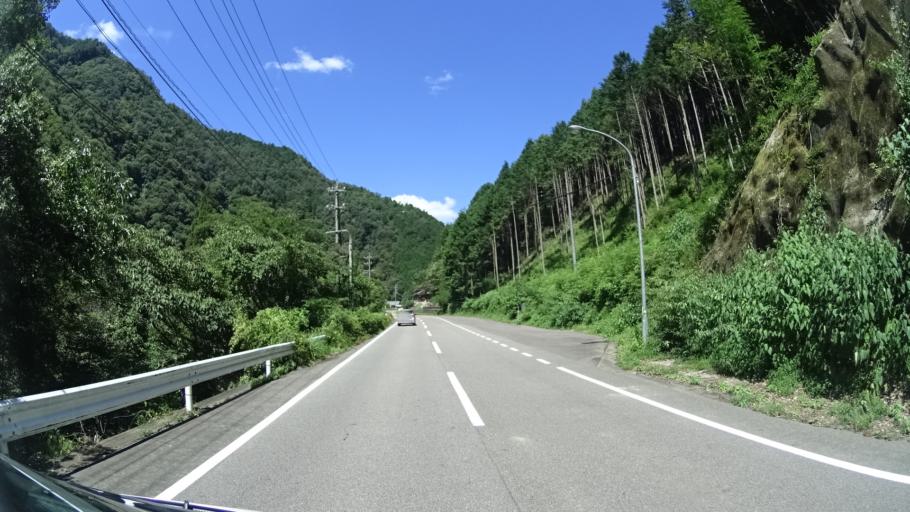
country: JP
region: Gifu
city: Minokamo
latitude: 35.5583
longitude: 137.1088
